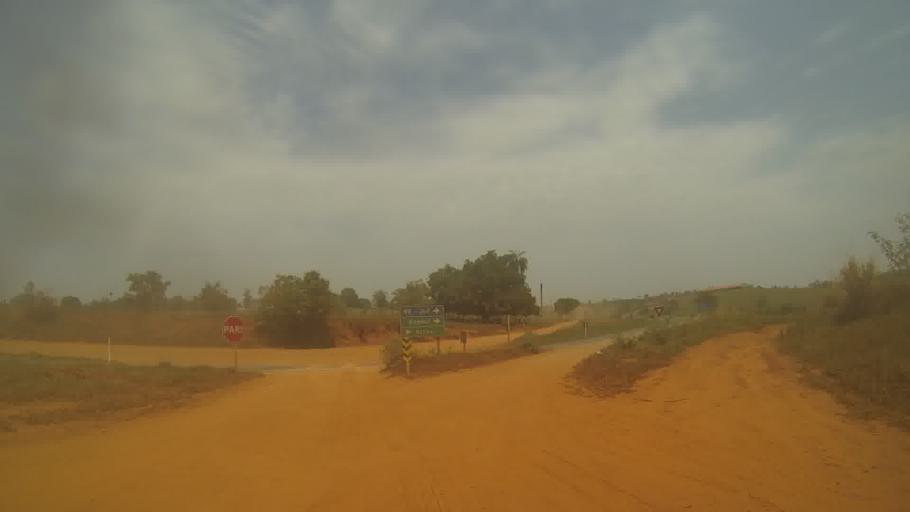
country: BR
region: Minas Gerais
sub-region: Bambui
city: Bambui
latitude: -20.0151
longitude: -45.9359
